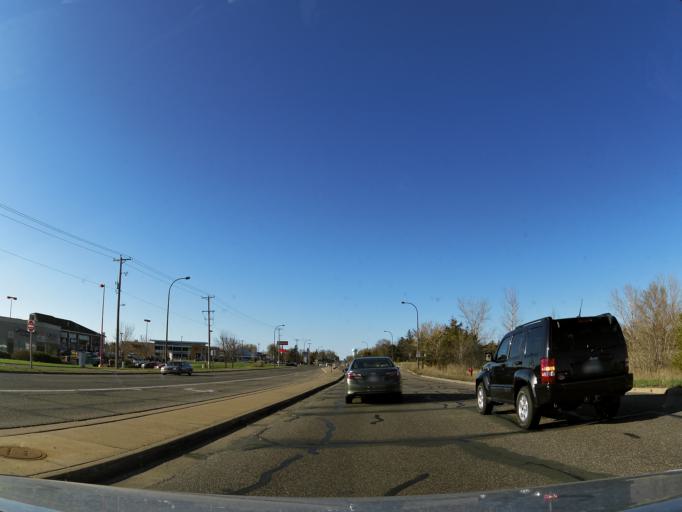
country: US
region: Wisconsin
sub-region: Saint Croix County
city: Hudson
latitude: 44.9653
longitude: -92.7211
